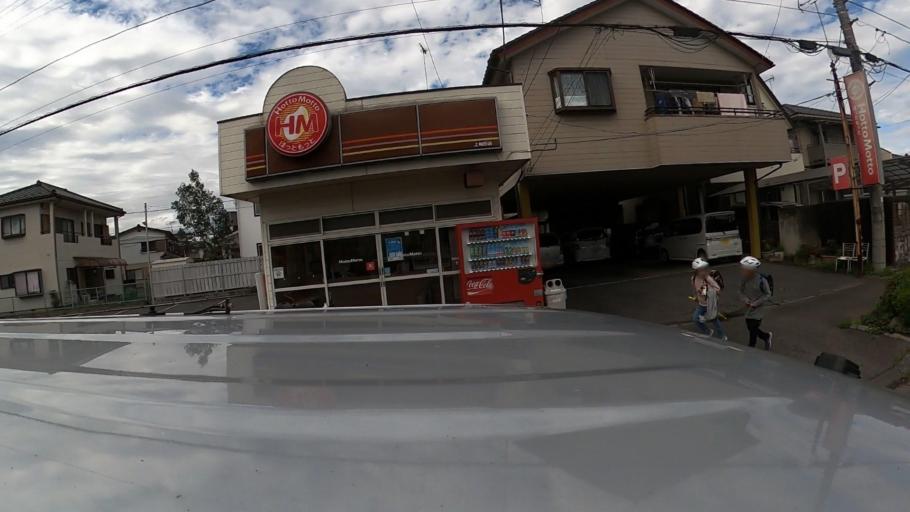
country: JP
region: Ibaraki
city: Ushiku
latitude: 35.9841
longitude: 140.1582
